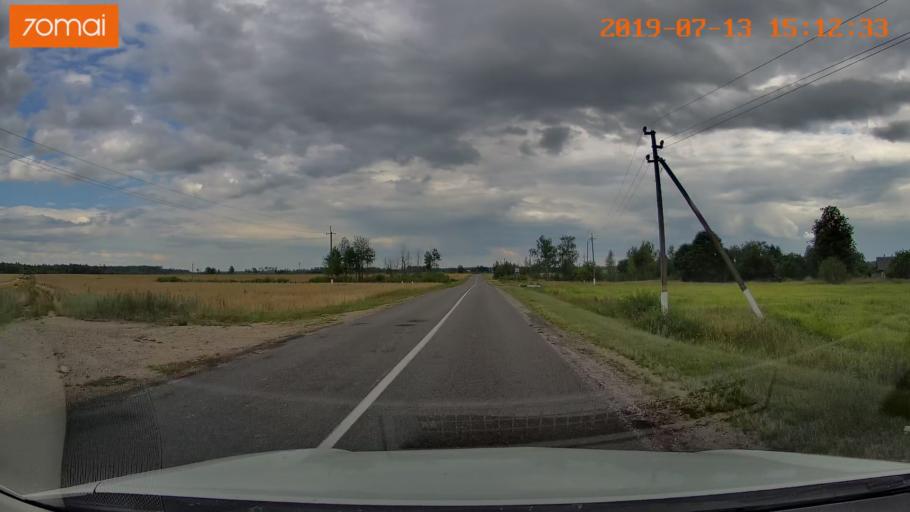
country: BY
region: Mogilev
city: Hlusha
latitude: 53.1474
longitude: 28.7936
